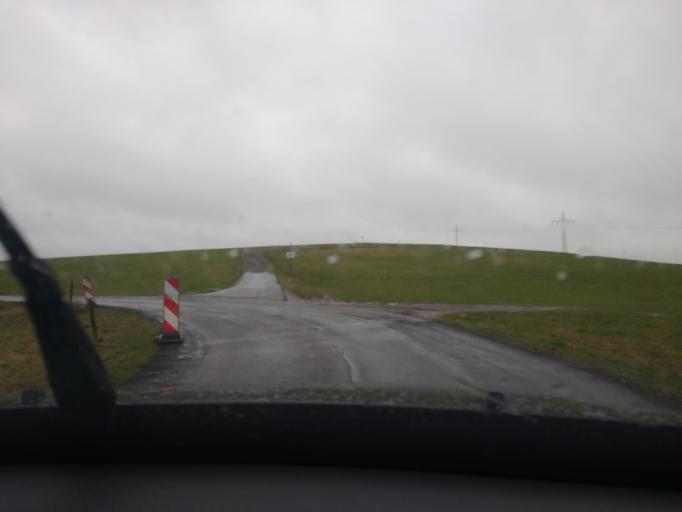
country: DE
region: Rheinland-Pfalz
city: Franzenheim
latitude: 49.6780
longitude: 6.6972
